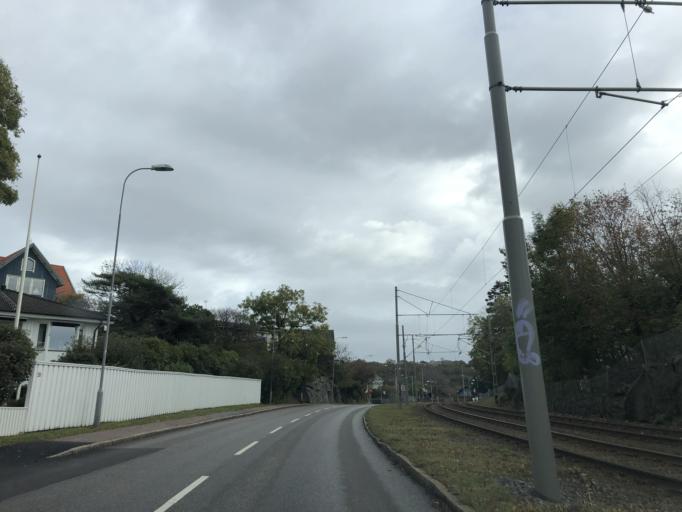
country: SE
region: Vaestra Goetaland
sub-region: Goteborg
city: Majorna
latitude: 57.6687
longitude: 11.8592
